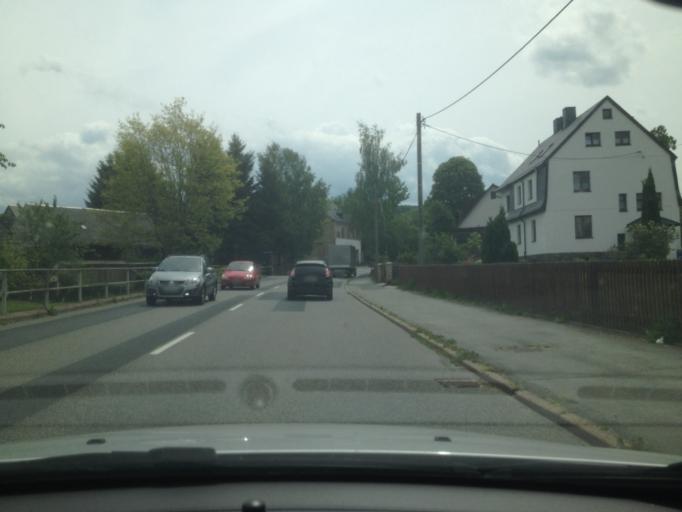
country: DE
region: Saxony
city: Stollberg
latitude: 50.6757
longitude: 12.7657
